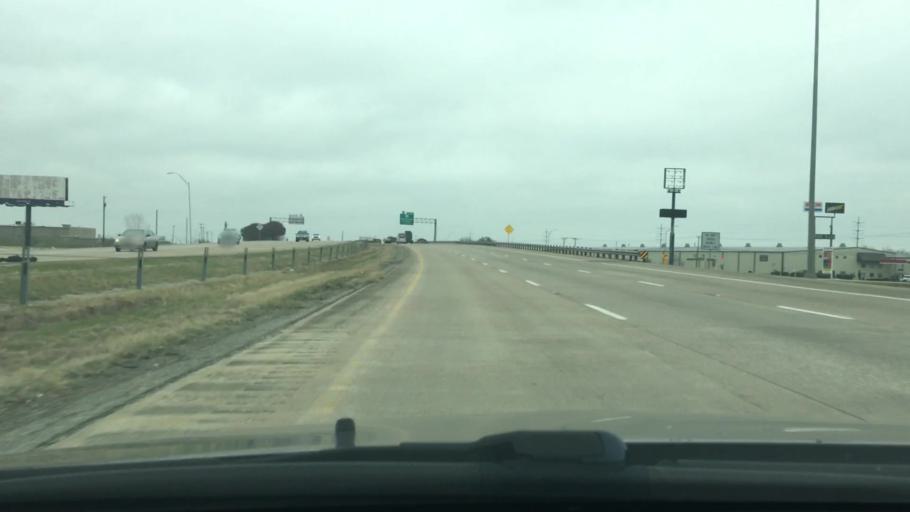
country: US
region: Texas
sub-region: Ellis County
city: Ennis
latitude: 32.3127
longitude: -96.5994
